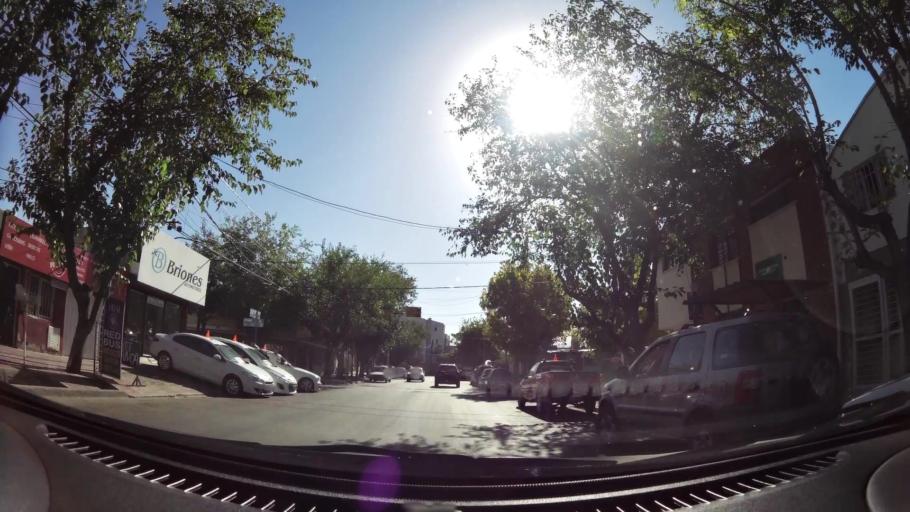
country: AR
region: Mendoza
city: Mendoza
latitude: -32.9017
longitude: -68.8140
